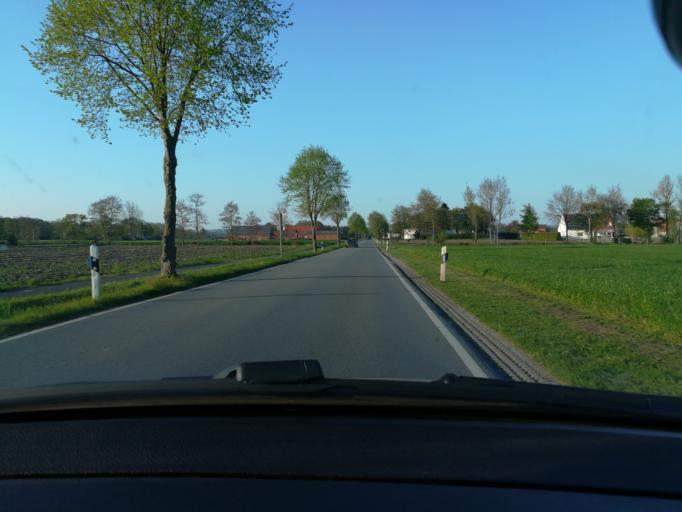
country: DE
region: North Rhine-Westphalia
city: Versmold
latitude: 52.0581
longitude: 8.1830
